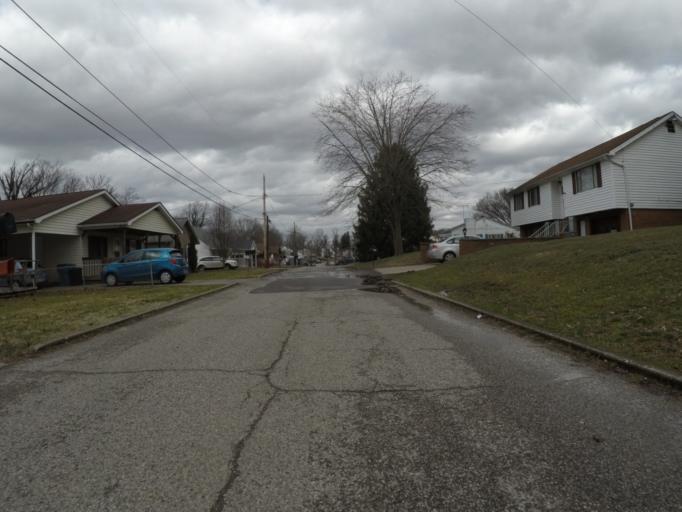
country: US
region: West Virginia
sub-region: Cabell County
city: Pea Ridge
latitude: 38.4067
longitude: -82.3801
